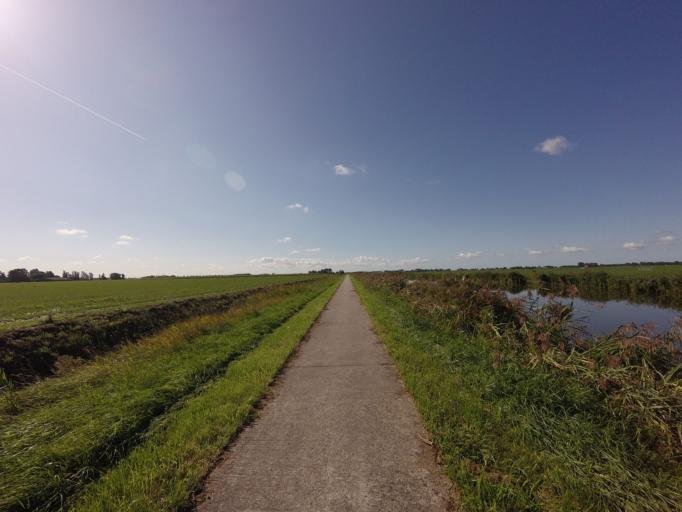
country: NL
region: Friesland
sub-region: Gemeente Boarnsterhim
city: Reduzum
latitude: 53.1362
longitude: 5.7598
